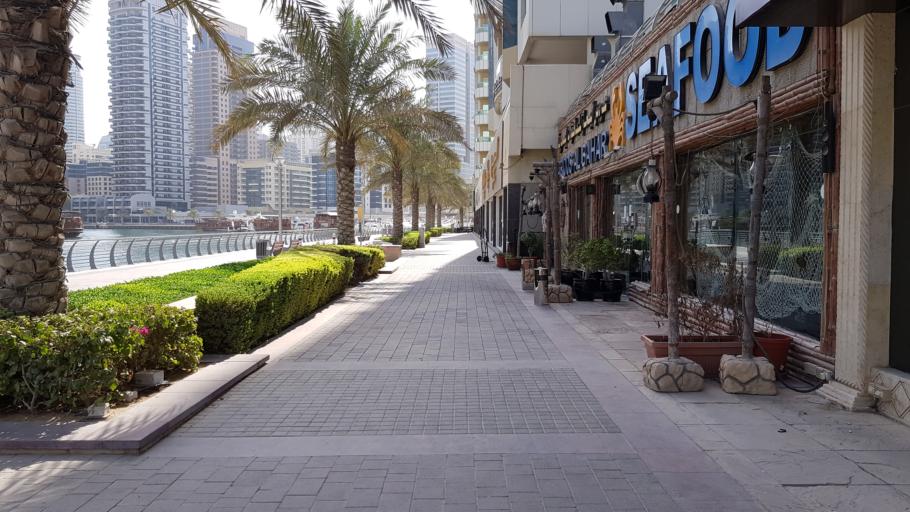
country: AE
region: Dubai
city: Dubai
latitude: 25.0701
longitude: 55.1288
